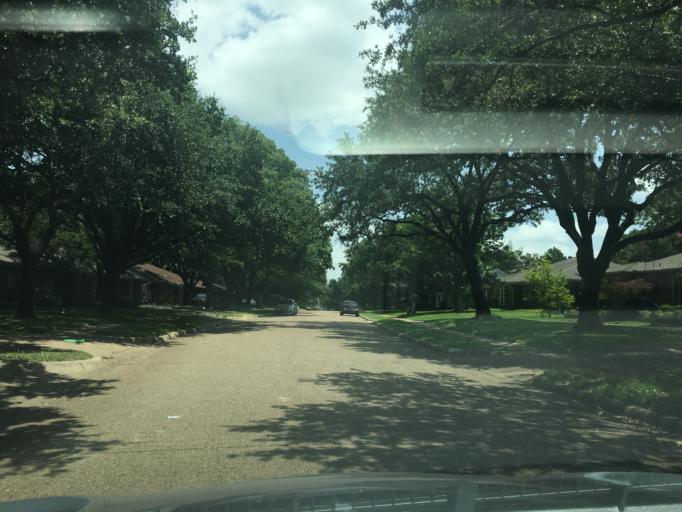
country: US
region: Texas
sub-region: Dallas County
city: University Park
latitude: 32.8853
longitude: -96.7822
